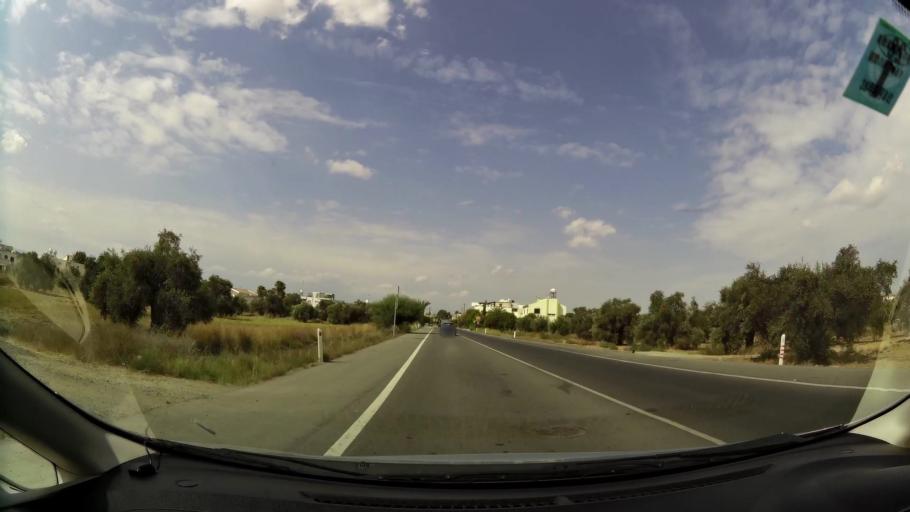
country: CY
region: Lefkosia
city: Tseri
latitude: 35.0683
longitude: 33.3311
